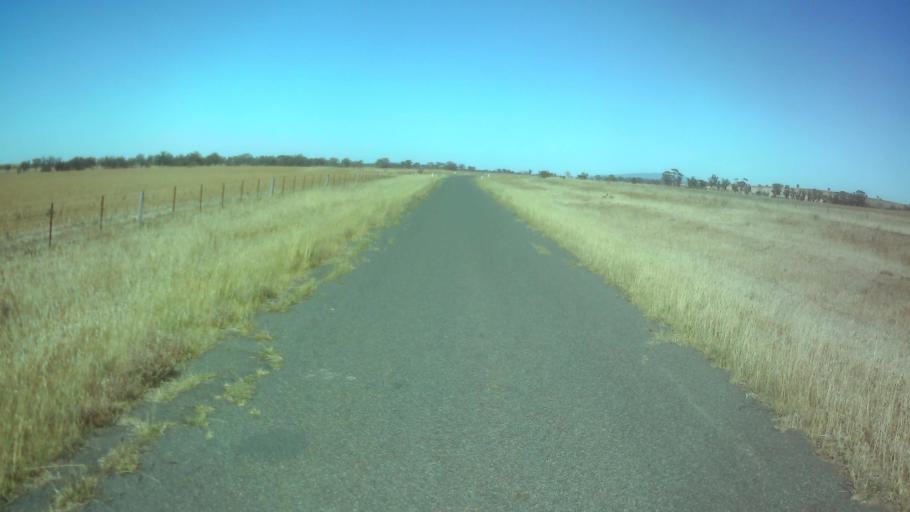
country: AU
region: New South Wales
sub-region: Weddin
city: Grenfell
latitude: -33.9959
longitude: 148.3860
